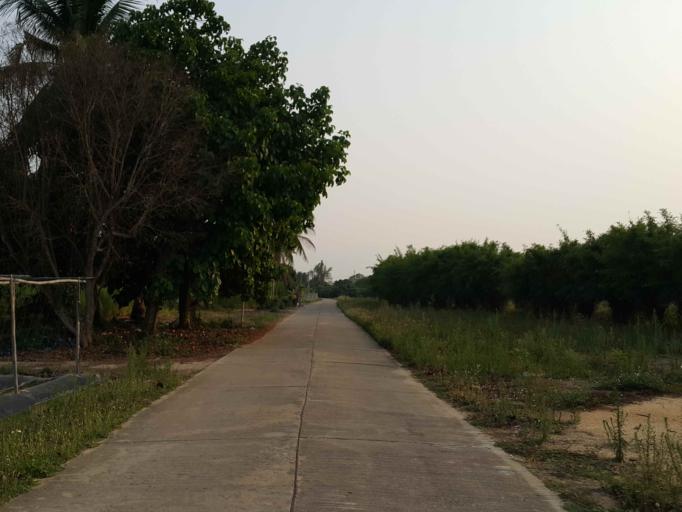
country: TH
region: Chiang Mai
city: Mae Taeng
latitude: 18.9932
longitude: 98.9814
